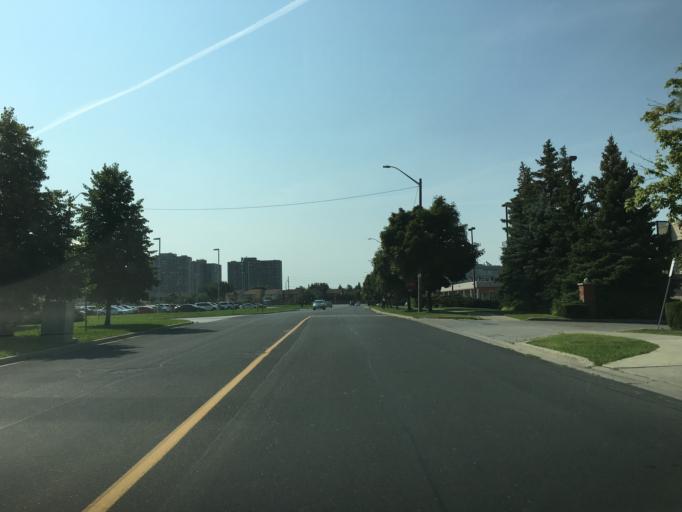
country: CA
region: Ontario
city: Markham
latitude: 43.8207
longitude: -79.3309
